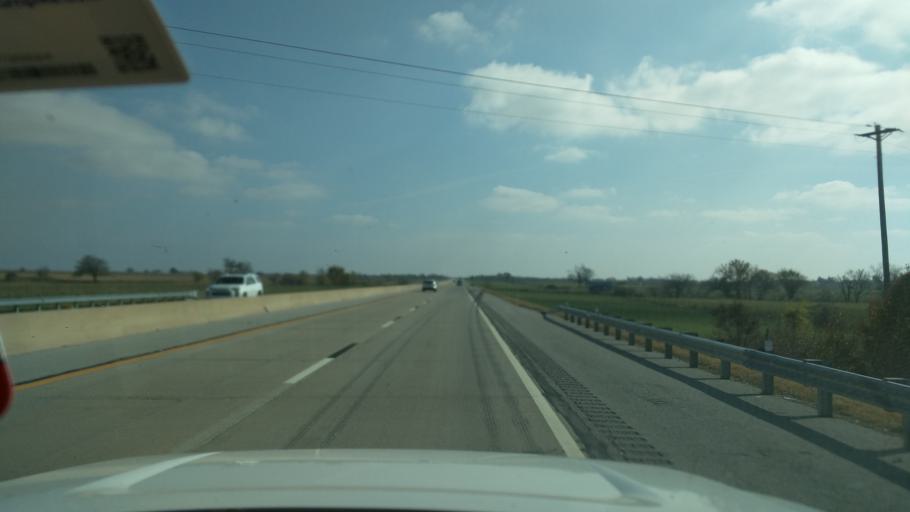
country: US
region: Oklahoma
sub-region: Wagoner County
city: Coweta
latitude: 35.9127
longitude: -95.5476
